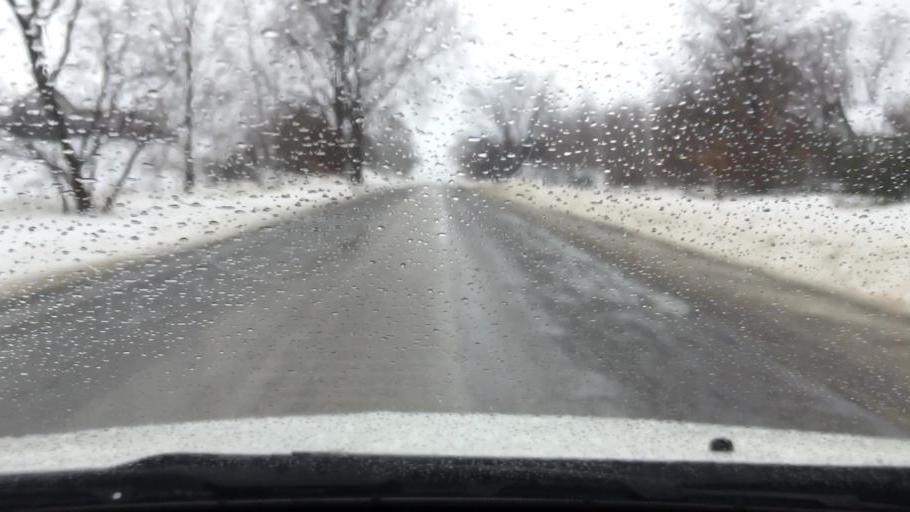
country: US
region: Michigan
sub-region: Charlevoix County
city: East Jordan
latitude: 45.1325
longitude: -85.1546
